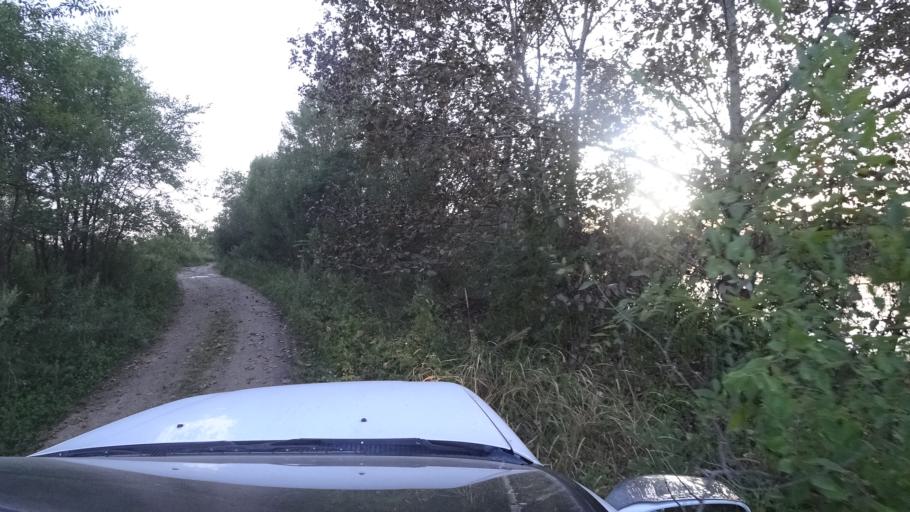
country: RU
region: Primorskiy
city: Dal'nerechensk
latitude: 45.9499
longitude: 133.7600
